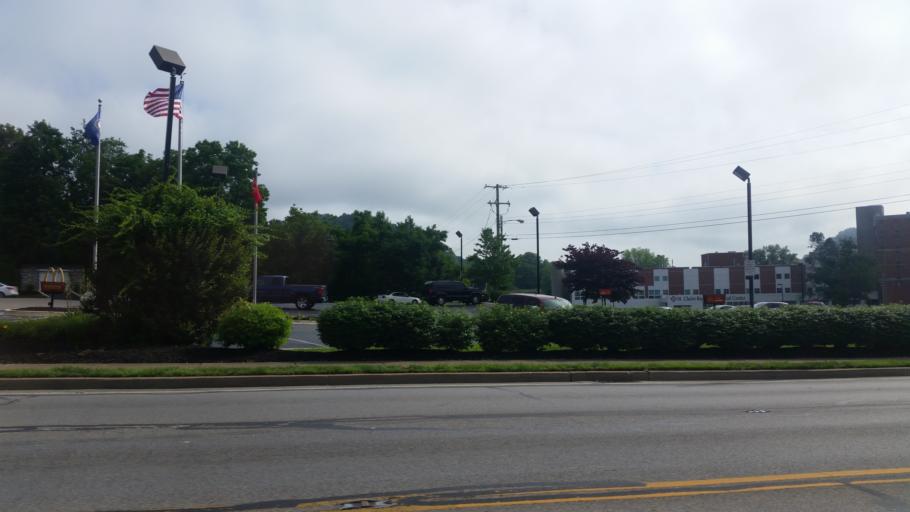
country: US
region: Kentucky
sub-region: Rowan County
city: Morehead
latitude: 38.1799
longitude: -83.4437
